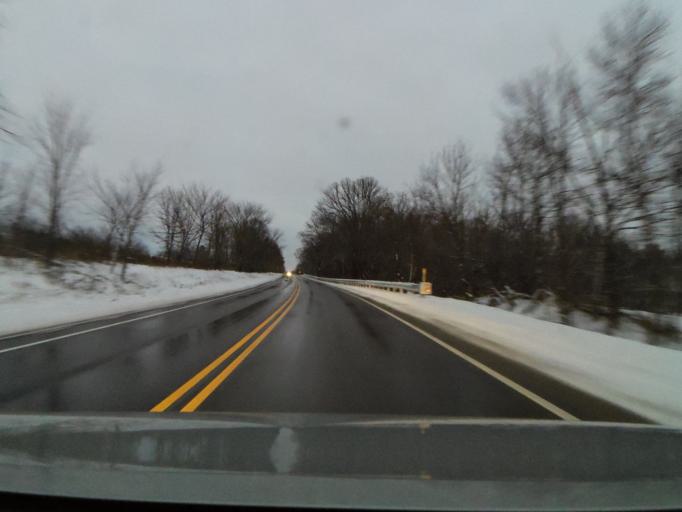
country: US
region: Wisconsin
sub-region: Dunn County
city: Boyceville
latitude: 44.9410
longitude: -92.0308
